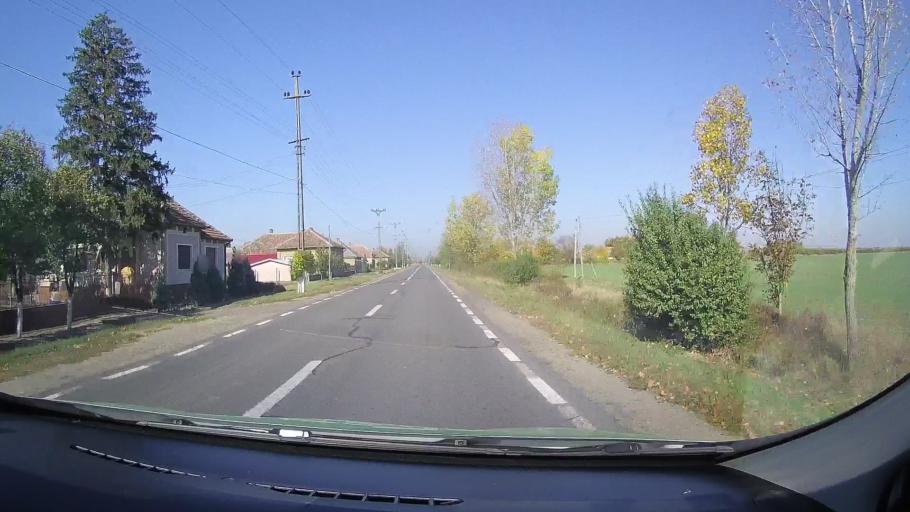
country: RO
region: Satu Mare
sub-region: Comuna Urziceni
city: Urziceni
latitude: 47.7259
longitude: 22.4104
